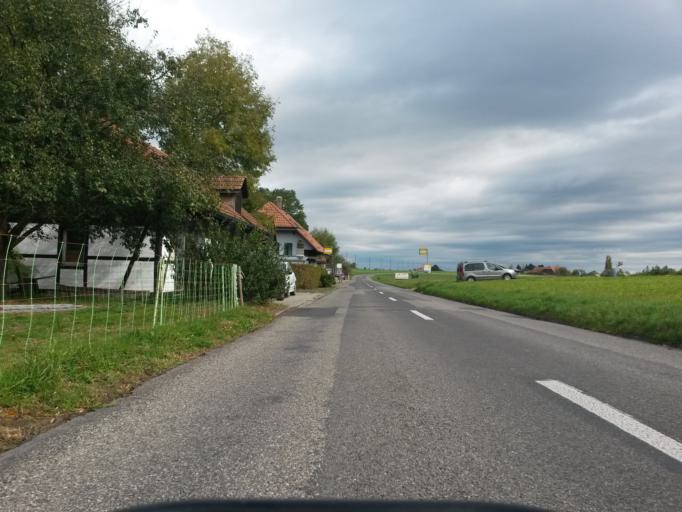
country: CH
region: Bern
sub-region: Seeland District
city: Leuzigen
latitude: 47.1421
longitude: 7.4855
